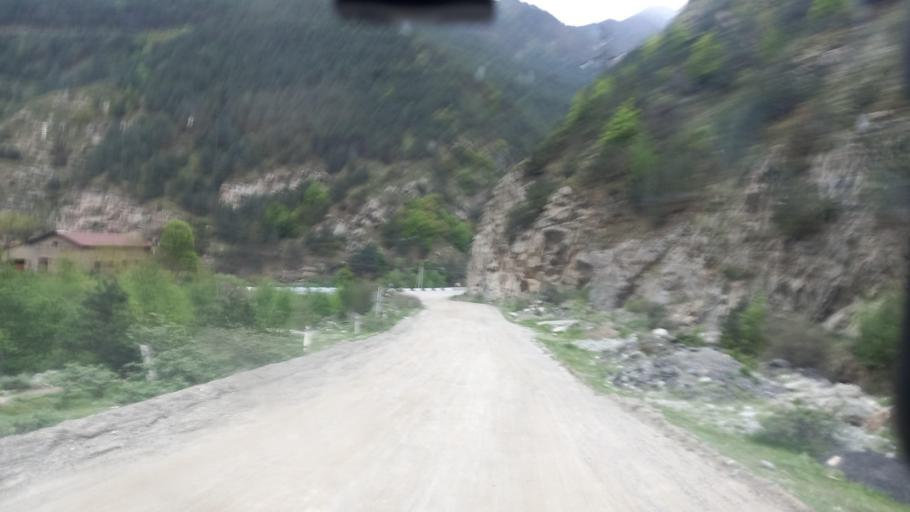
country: RU
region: North Ossetia
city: Mizur
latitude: 42.8403
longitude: 44.0265
